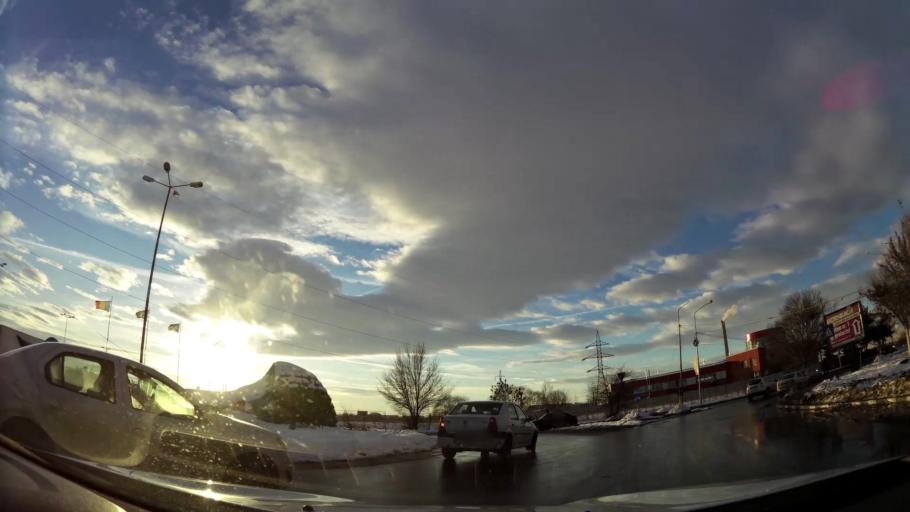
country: RO
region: Ilfov
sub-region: Comuna Popesti-Leordeni
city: Popesti-Leordeni
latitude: 44.3648
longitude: 26.1264
